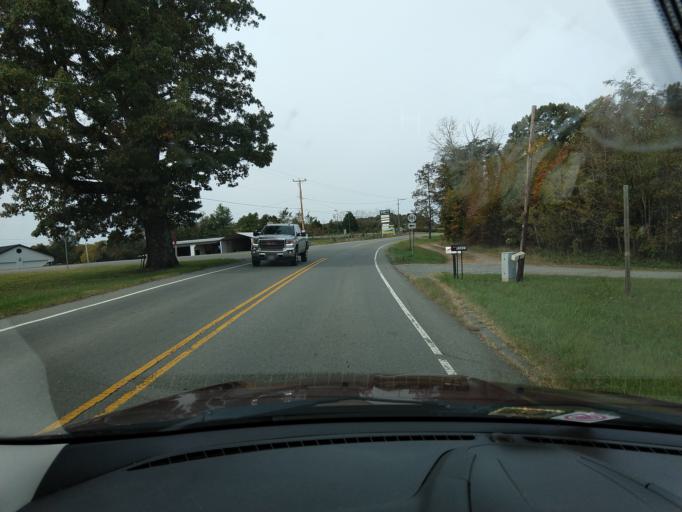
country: US
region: Virginia
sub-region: Franklin County
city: Union Hall
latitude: 36.9938
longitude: -79.6852
